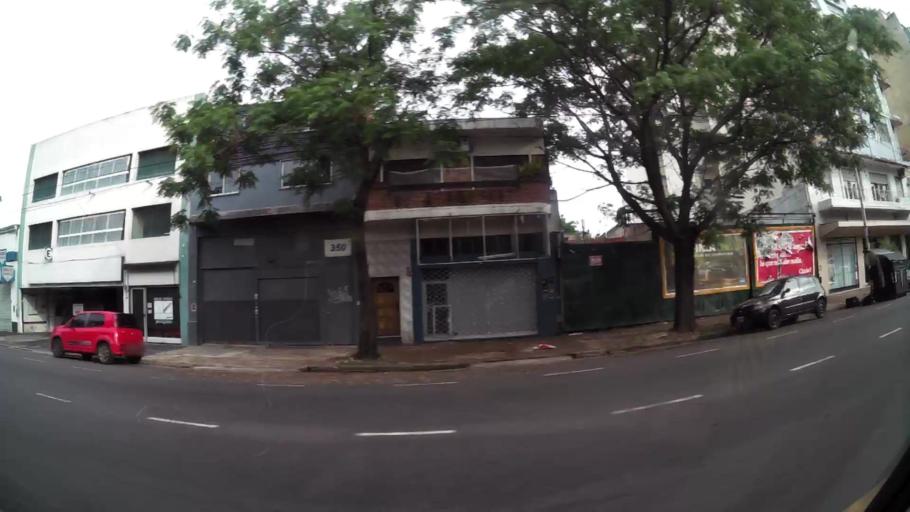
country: AR
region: Buenos Aires F.D.
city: Villa Santa Rita
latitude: -34.6327
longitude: -58.4308
